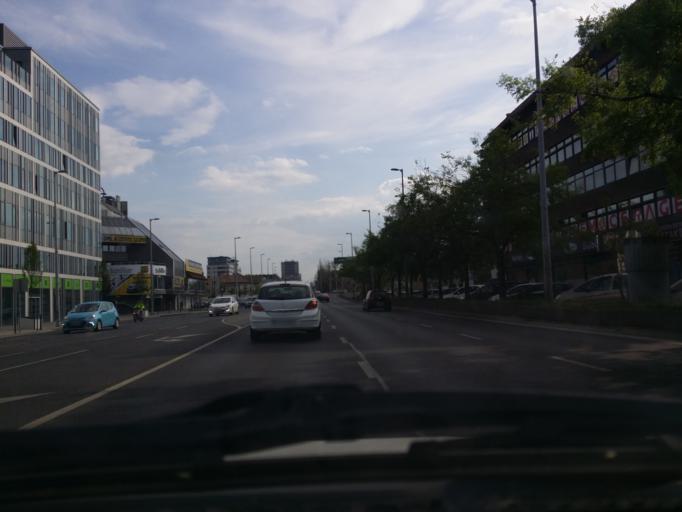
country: HU
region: Budapest
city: Budapest XIII. keruelet
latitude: 47.5449
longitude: 19.0717
